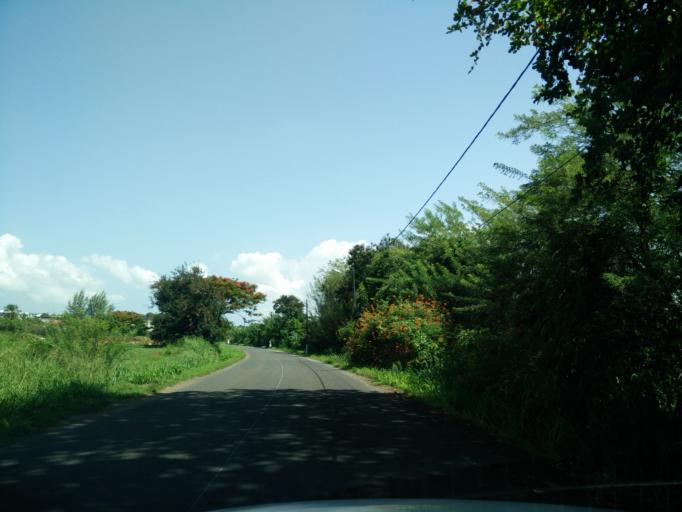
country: GP
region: Guadeloupe
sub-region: Guadeloupe
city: Petit-Bourg
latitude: 16.1757
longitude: -61.5868
